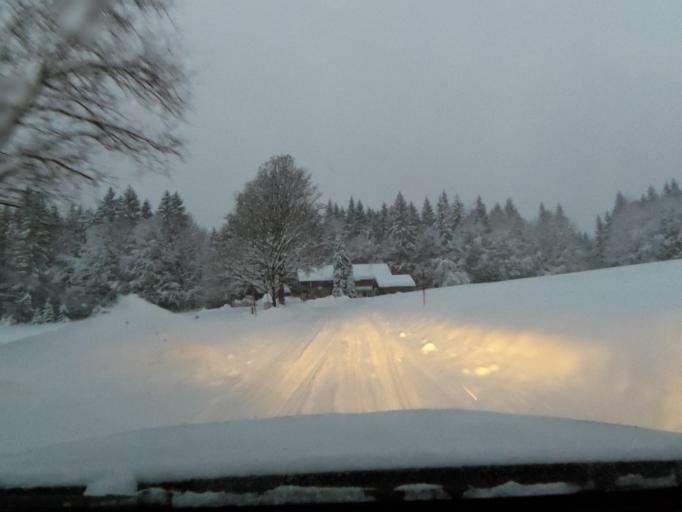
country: DE
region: Bavaria
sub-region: Lower Bavaria
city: Neuschonau
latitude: 48.9271
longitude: 13.4286
